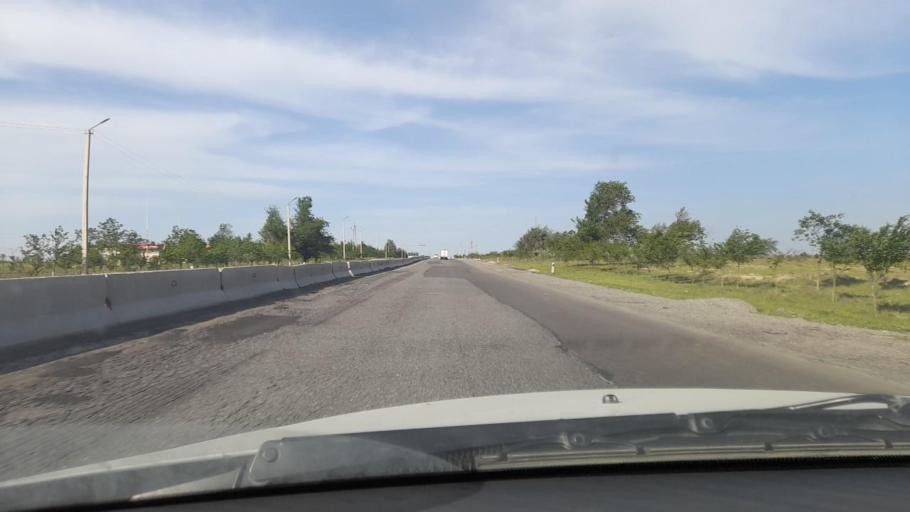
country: UZ
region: Samarqand
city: Bulung'ur
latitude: 39.8429
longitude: 67.4527
